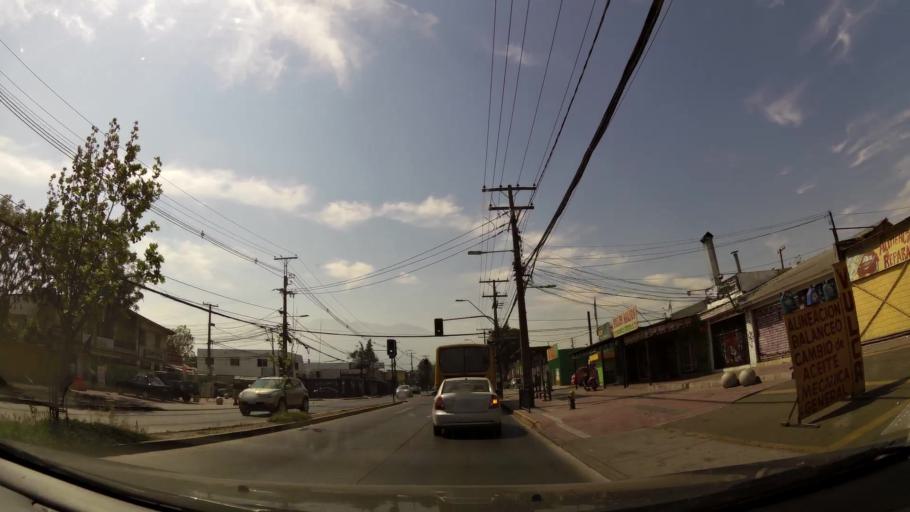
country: CL
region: Santiago Metropolitan
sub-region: Provincia de Cordillera
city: Puente Alto
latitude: -33.5801
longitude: -70.5877
